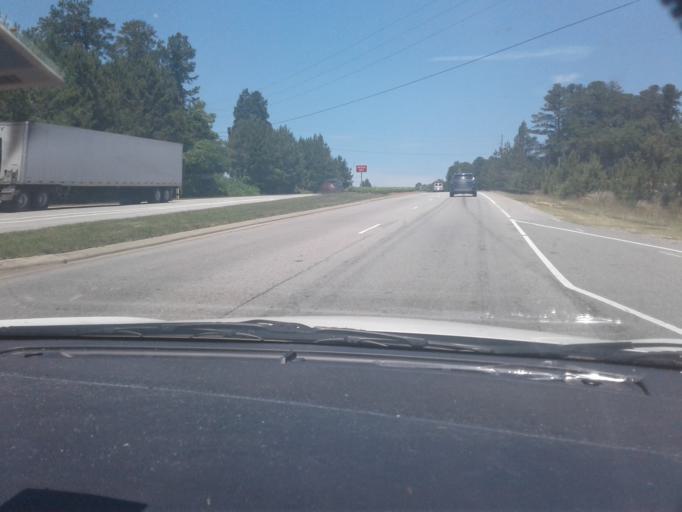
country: US
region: North Carolina
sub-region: Wake County
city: Holly Springs
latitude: 35.6238
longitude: -78.8191
